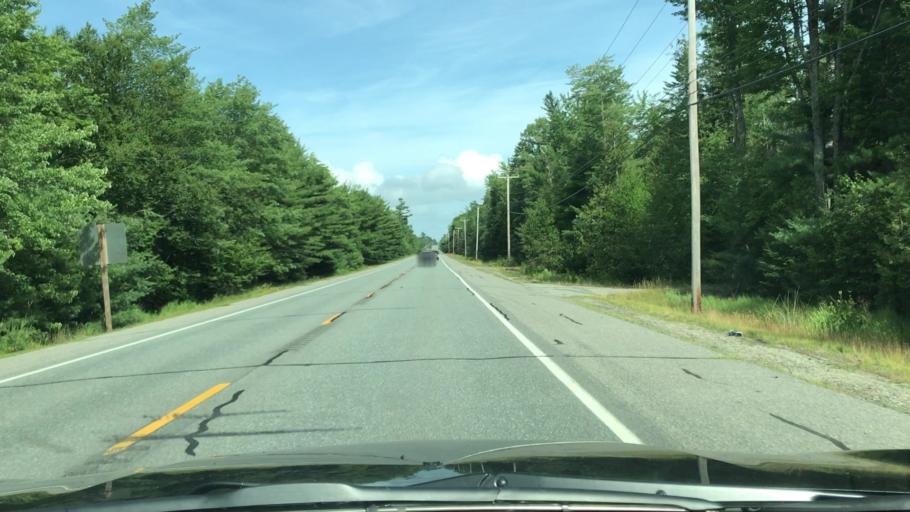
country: US
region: Maine
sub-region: Hancock County
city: Ellsworth
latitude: 44.5396
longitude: -68.4697
